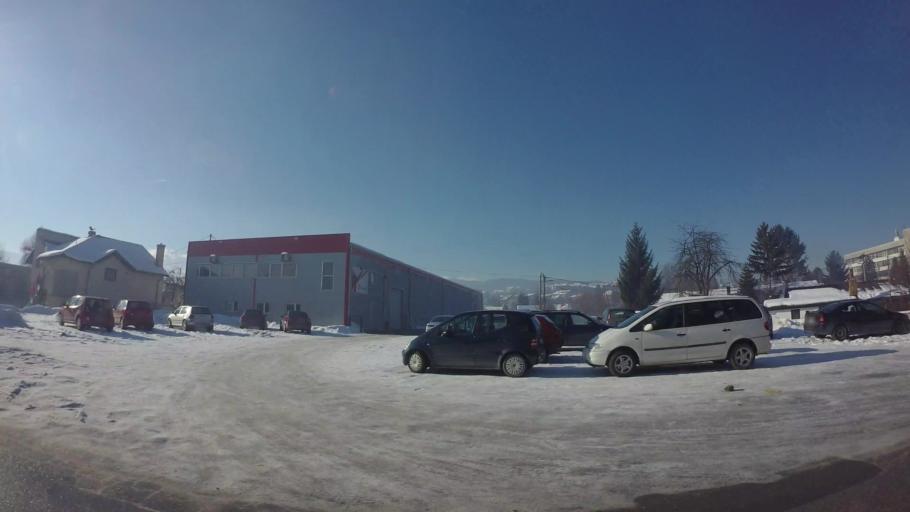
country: BA
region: Federation of Bosnia and Herzegovina
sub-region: Kanton Sarajevo
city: Sarajevo
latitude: 43.8230
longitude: 18.3766
